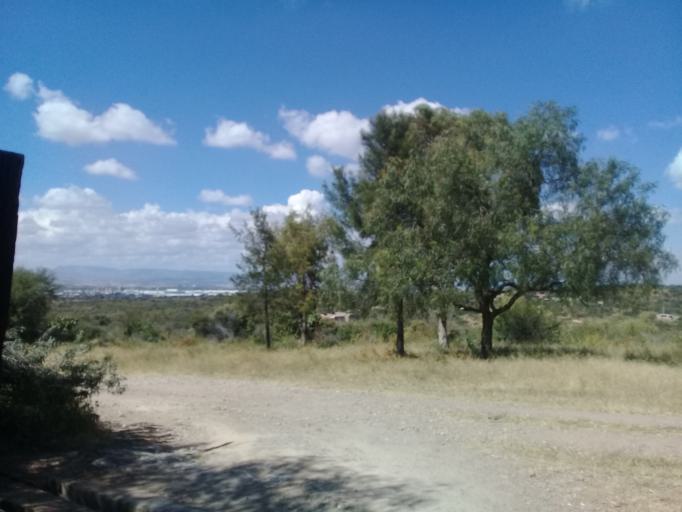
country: MX
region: Aguascalientes
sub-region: Aguascalientes
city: San Sebastian [Fraccionamiento]
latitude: 21.7828
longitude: -102.2519
